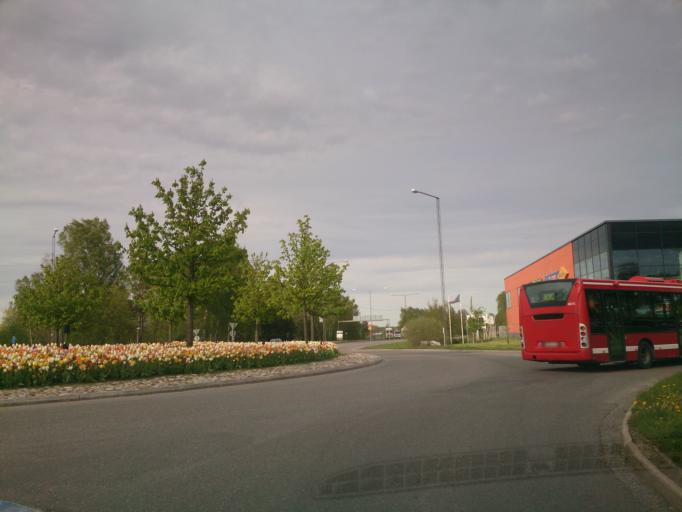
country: SE
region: Stockholm
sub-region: Haninge Kommun
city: Handen
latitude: 59.1755
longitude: 18.1416
